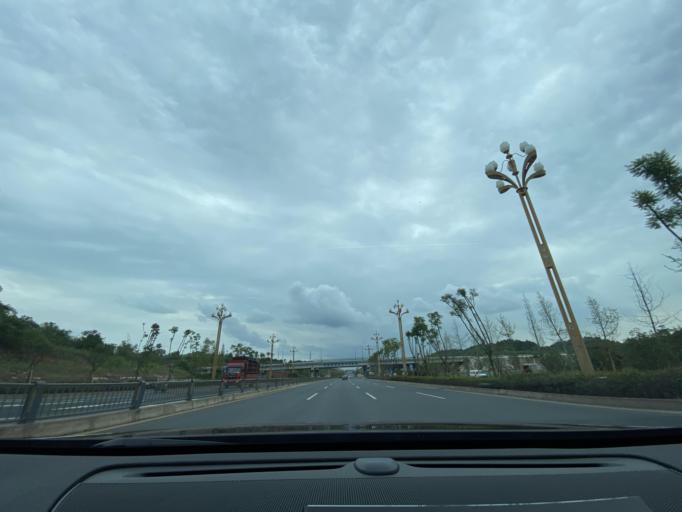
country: CN
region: Sichuan
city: Jiancheng
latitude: 30.4631
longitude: 104.4956
